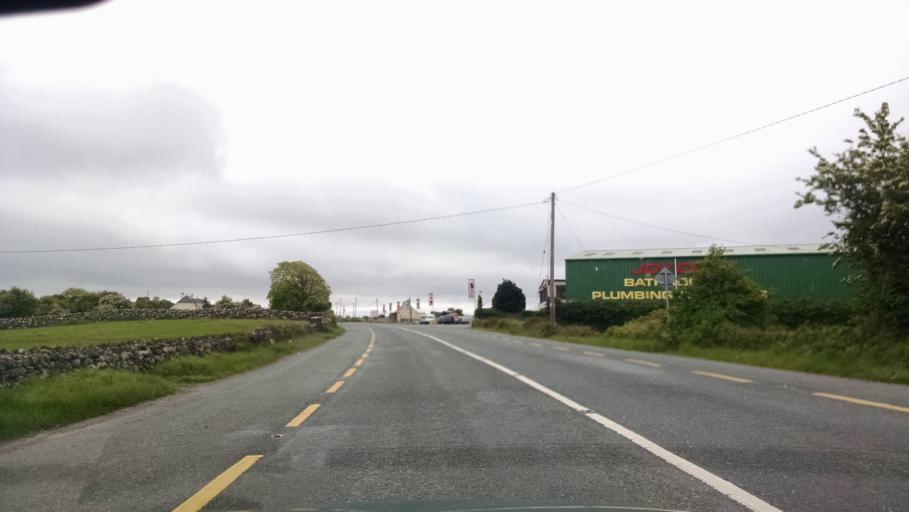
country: IE
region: Connaught
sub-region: County Galway
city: Moycullen
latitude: 53.4638
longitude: -9.1047
